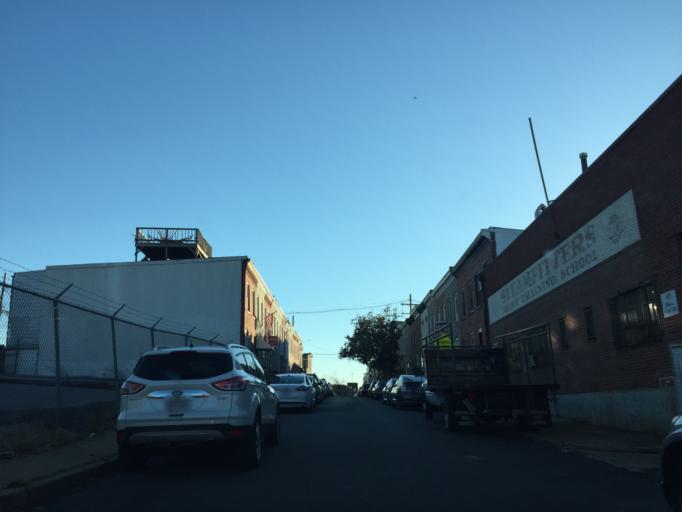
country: US
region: Maryland
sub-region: City of Baltimore
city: Baltimore
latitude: 39.2716
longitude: -76.5976
